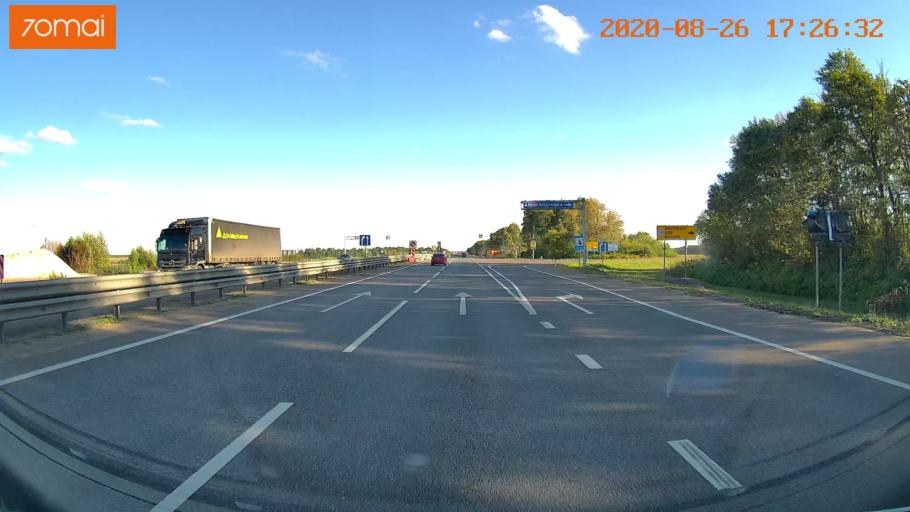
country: RU
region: Tula
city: Kazachka
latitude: 53.4855
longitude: 38.1177
